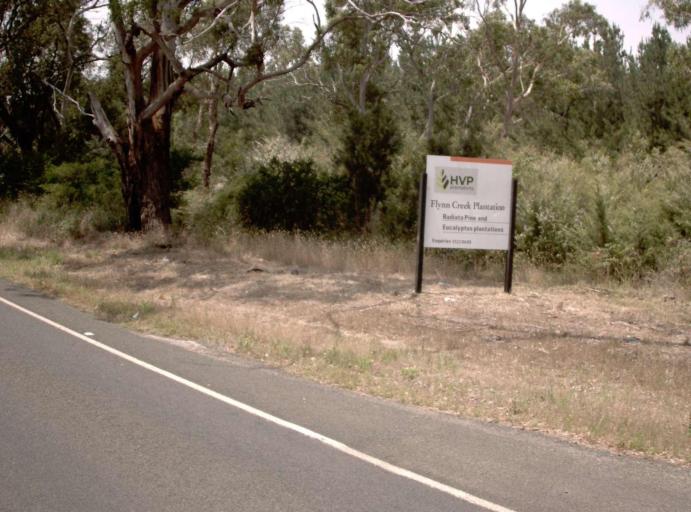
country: AU
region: Victoria
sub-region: Latrobe
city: Traralgon
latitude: -38.2504
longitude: 146.6579
